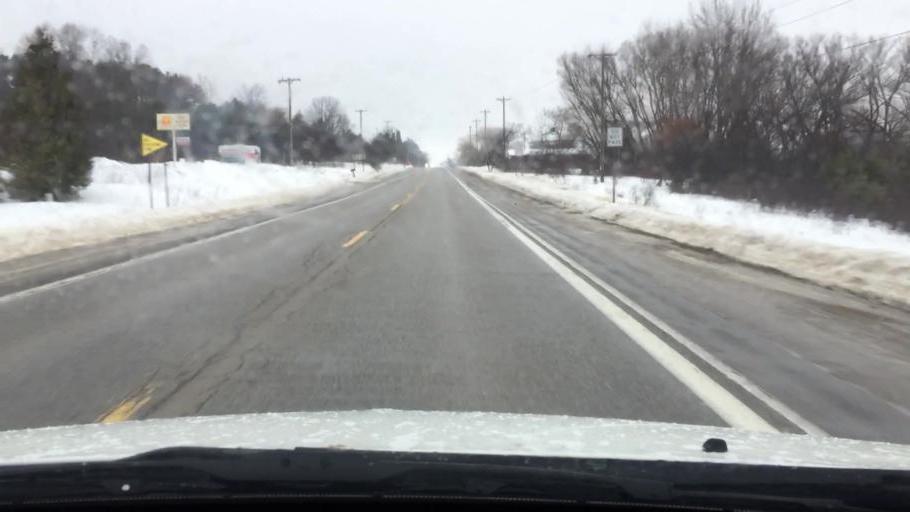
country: US
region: Michigan
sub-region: Charlevoix County
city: East Jordan
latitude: 45.1371
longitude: -85.1397
